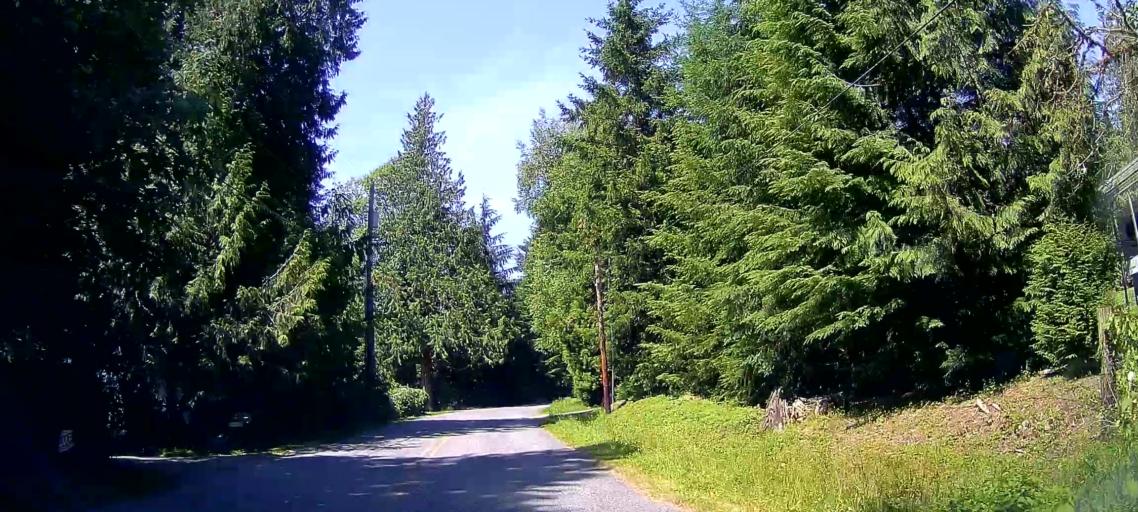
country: US
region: Washington
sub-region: Whatcom County
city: Sudden Valley
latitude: 48.6123
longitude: -122.3188
